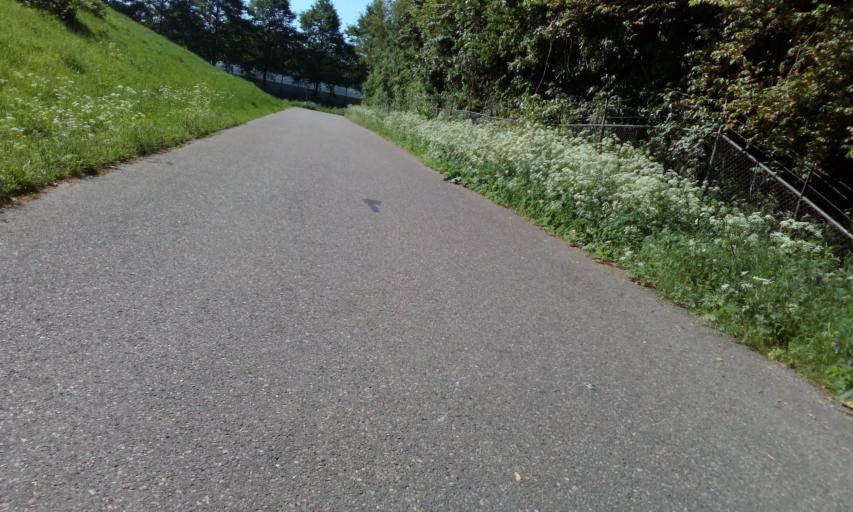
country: NL
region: South Holland
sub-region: Gemeente Rotterdam
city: Rotterdam
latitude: 51.9476
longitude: 4.5077
